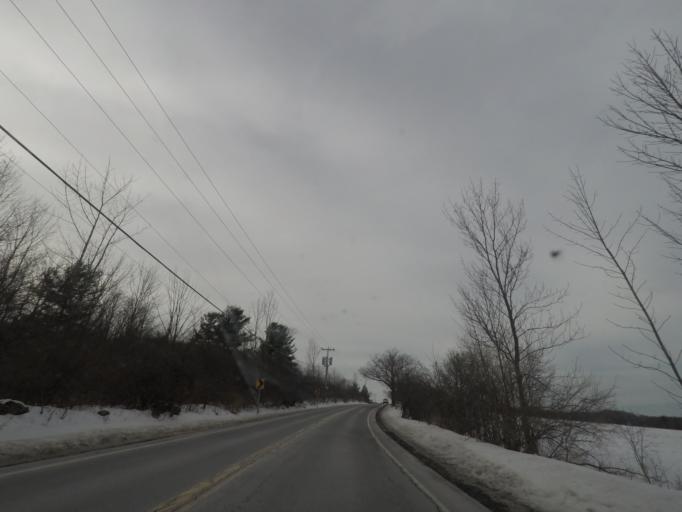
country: US
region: New York
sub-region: Albany County
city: Altamont
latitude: 42.6766
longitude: -74.0808
